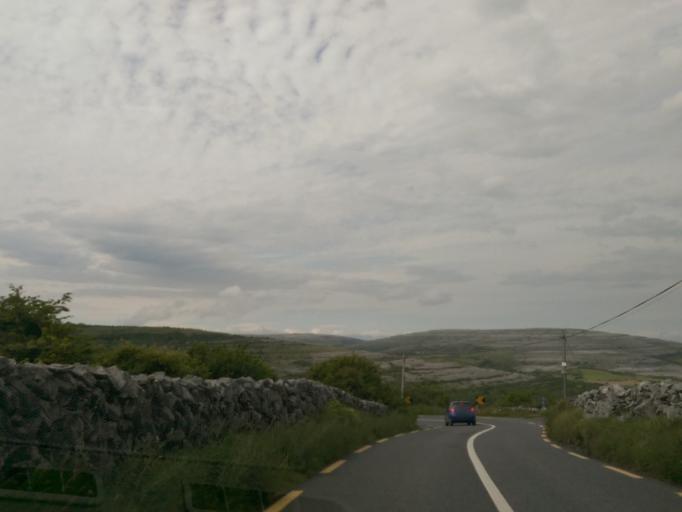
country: IE
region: Connaught
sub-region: County Galway
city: Bearna
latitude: 53.0693
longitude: -9.1840
